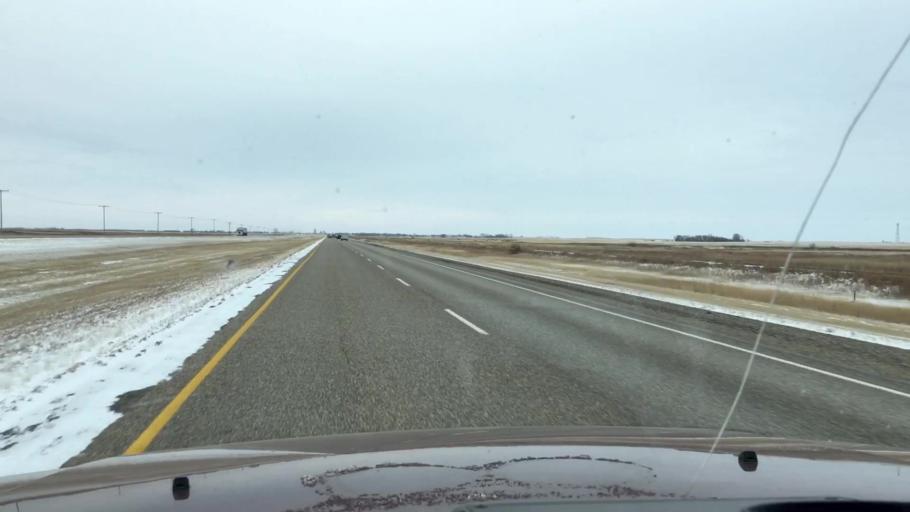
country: CA
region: Saskatchewan
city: Watrous
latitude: 51.0871
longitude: -105.8547
